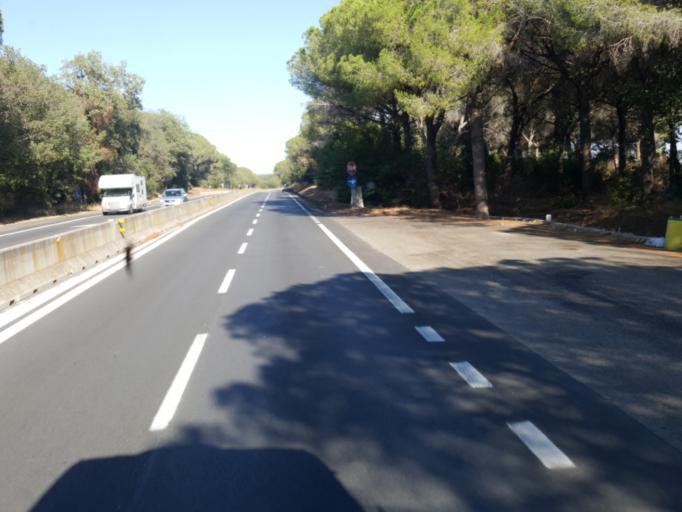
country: IT
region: Latium
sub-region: Provincia di Viterbo
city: Pescia Romana
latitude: 42.4141
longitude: 11.4658
